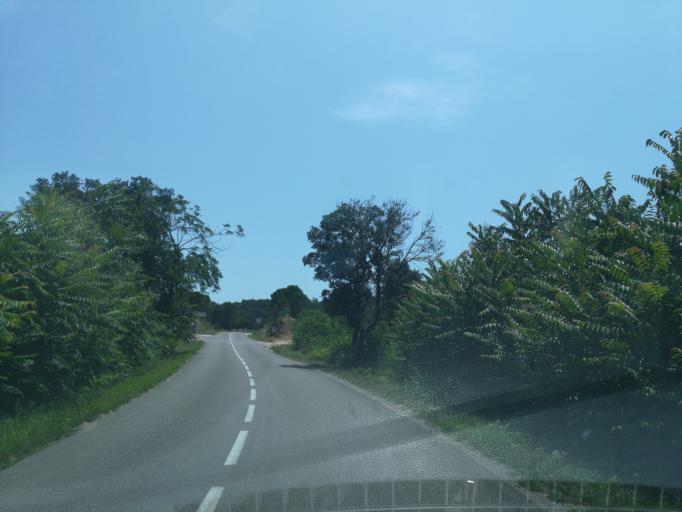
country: ES
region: Catalonia
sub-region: Provincia de Girona
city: Agullana
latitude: 42.3908
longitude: 2.8519
